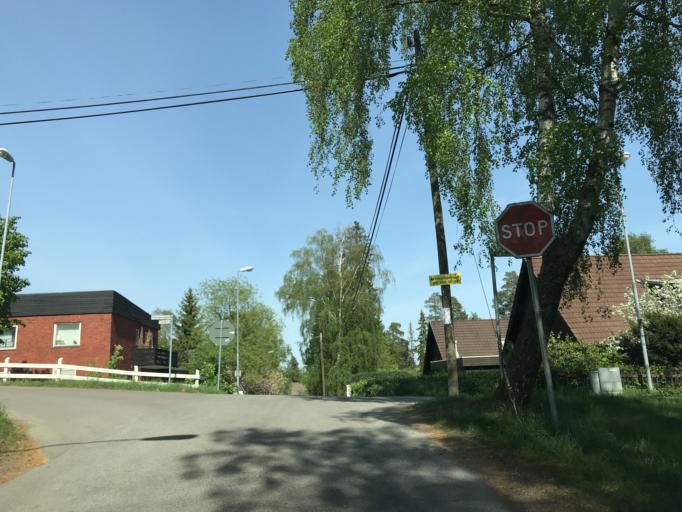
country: SE
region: Stockholm
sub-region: Sollentuna Kommun
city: Sollentuna
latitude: 59.4222
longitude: 17.9680
